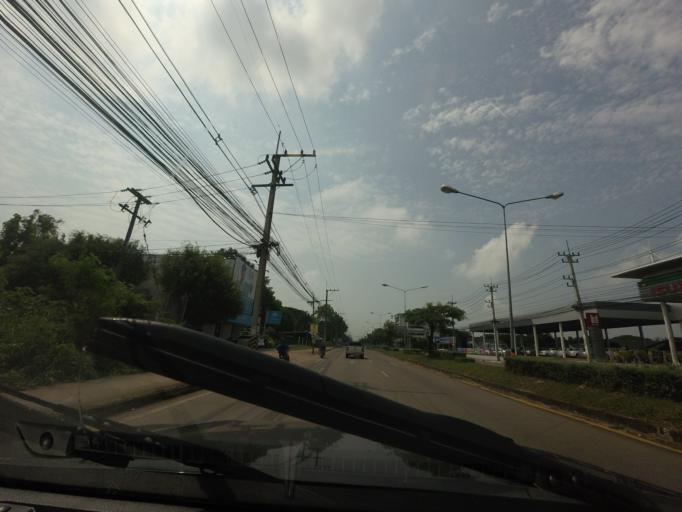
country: TH
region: Phrae
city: Phrae
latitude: 18.1247
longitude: 100.1419
